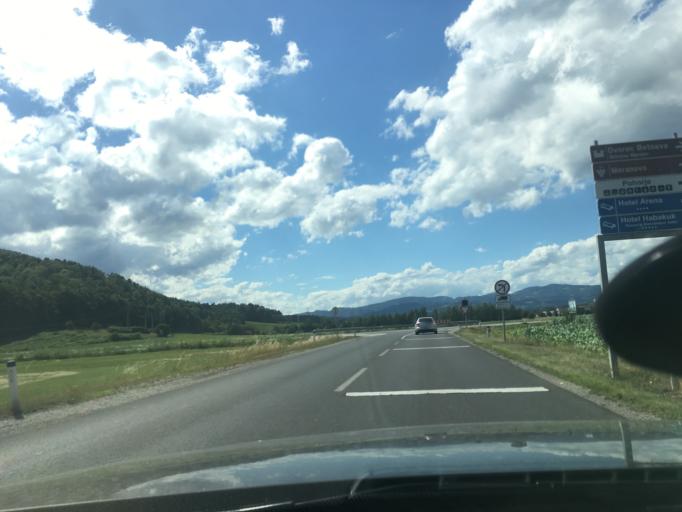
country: SI
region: Maribor
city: Razvanje
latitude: 46.5272
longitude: 15.6384
